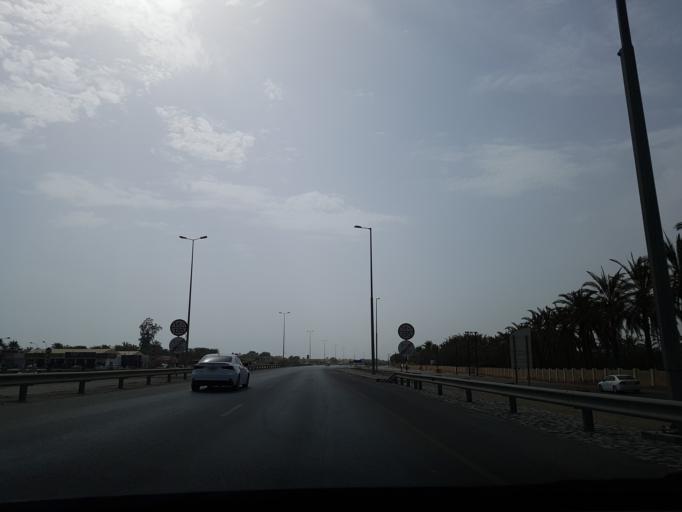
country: OM
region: Al Batinah
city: Saham
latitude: 24.1325
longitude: 56.8896
